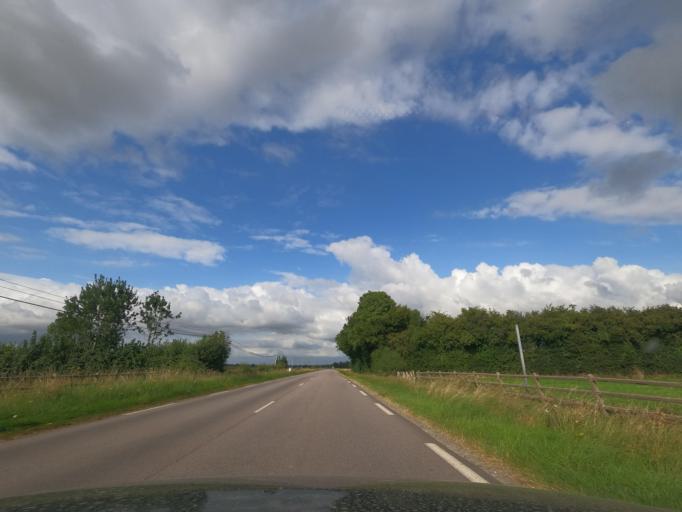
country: FR
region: Haute-Normandie
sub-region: Departement de l'Eure
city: Broglie
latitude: 48.9895
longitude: 0.5016
